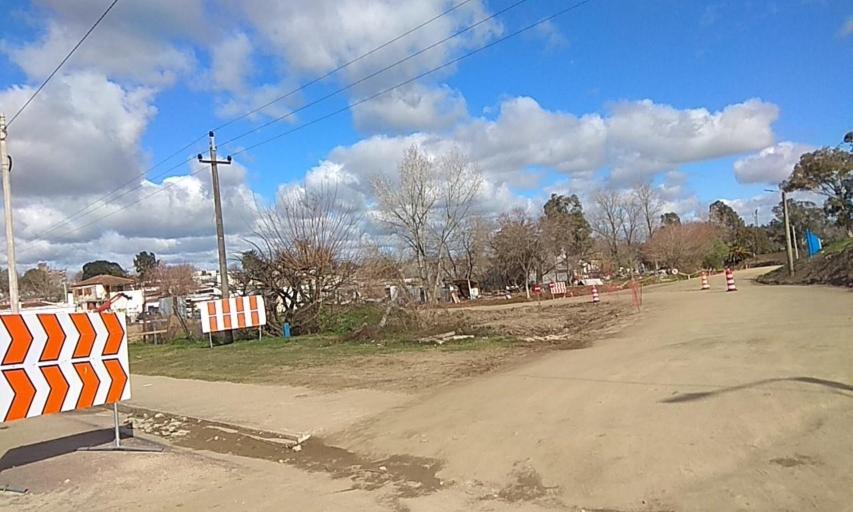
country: UY
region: Florida
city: Florida
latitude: -34.0890
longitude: -56.2214
